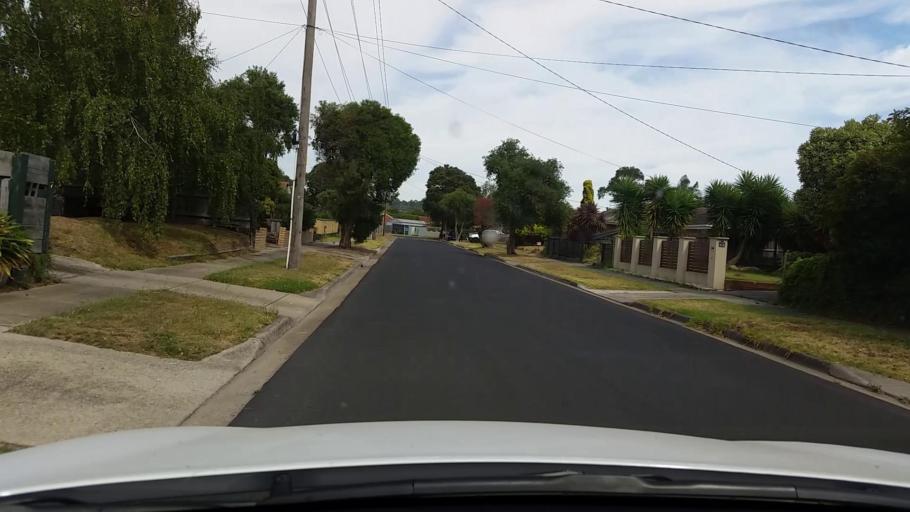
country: AU
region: Victoria
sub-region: Mornington Peninsula
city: Tyabb
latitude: -38.2553
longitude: 145.1887
